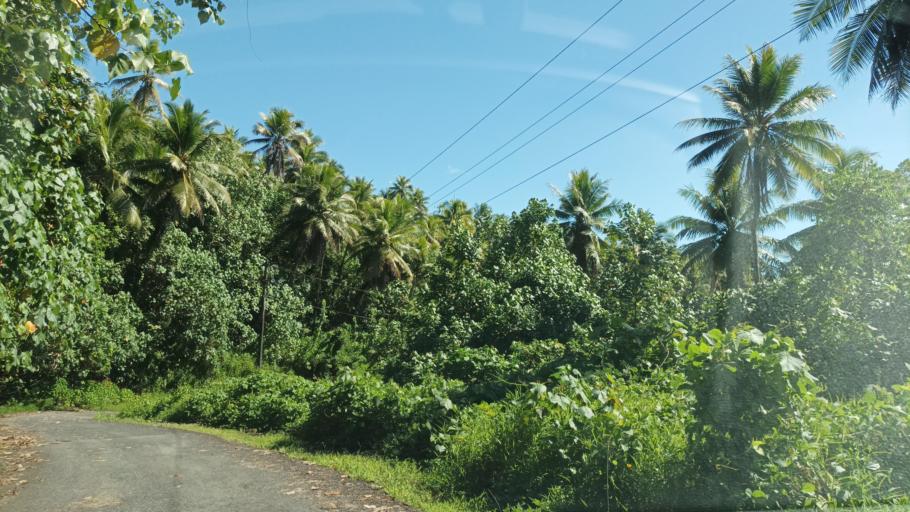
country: FM
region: Pohnpei
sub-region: Madolenihm Municipality
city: Madolenihm Municipality Government
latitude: 6.8494
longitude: 158.3180
